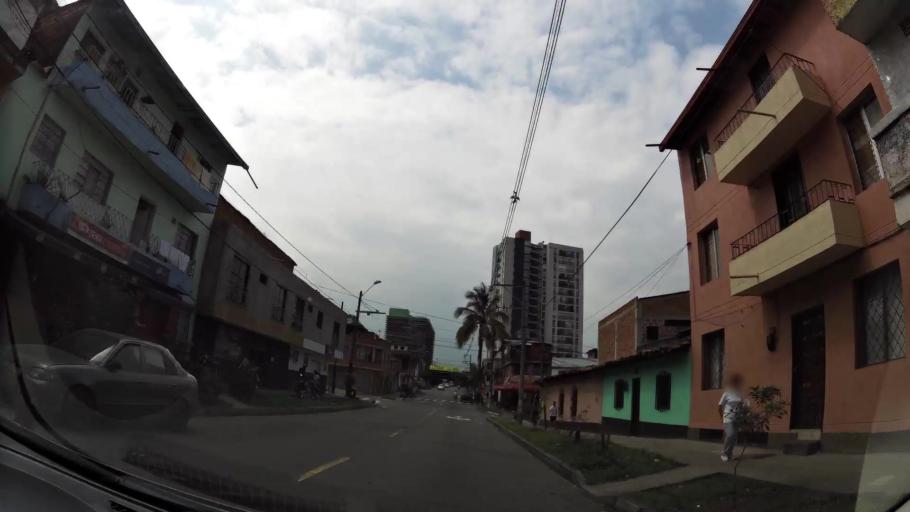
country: CO
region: Antioquia
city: Medellin
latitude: 6.2702
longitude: -75.5586
